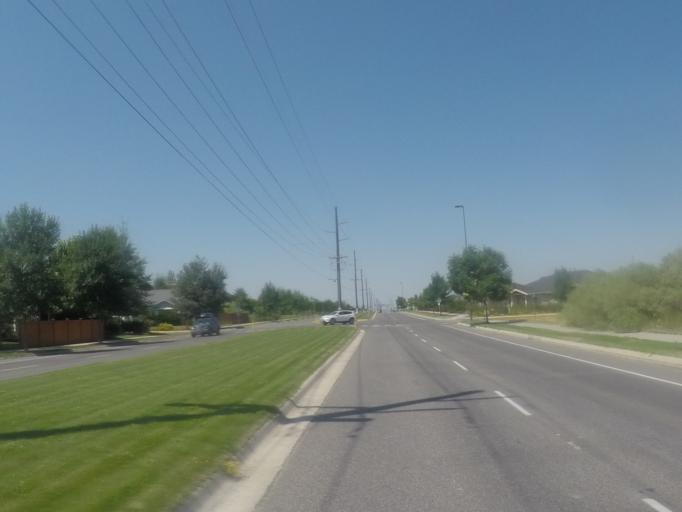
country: US
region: Montana
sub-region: Gallatin County
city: Bozeman
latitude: 45.6930
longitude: -111.0763
